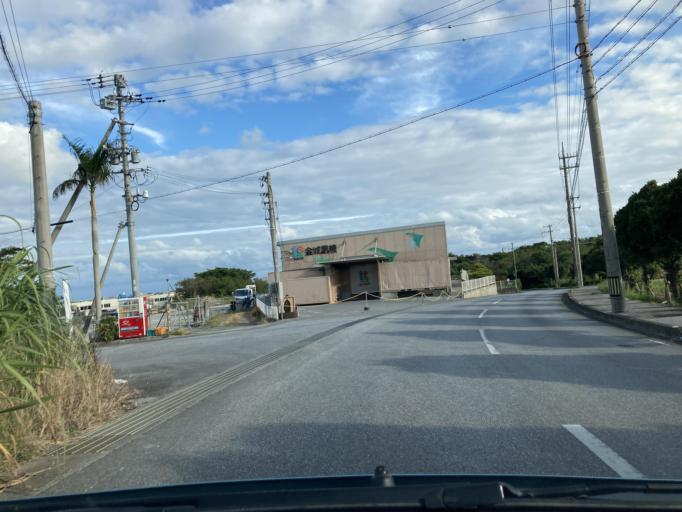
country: JP
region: Okinawa
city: Itoman
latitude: 26.1350
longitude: 127.7496
